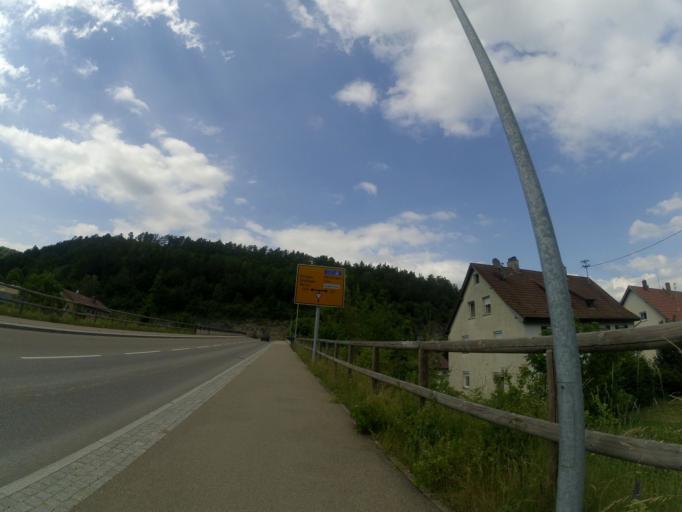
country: DE
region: Baden-Wuerttemberg
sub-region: Tuebingen Region
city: Blaubeuren
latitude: 48.4022
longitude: 9.7842
